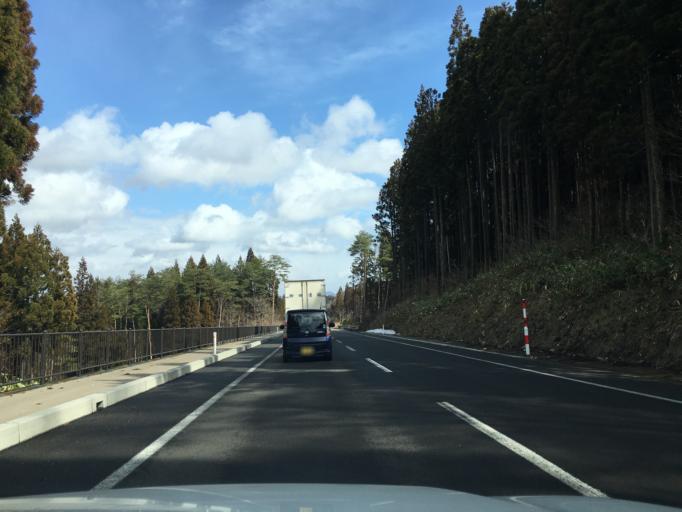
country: JP
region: Akita
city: Takanosu
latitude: 40.1085
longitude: 140.3557
